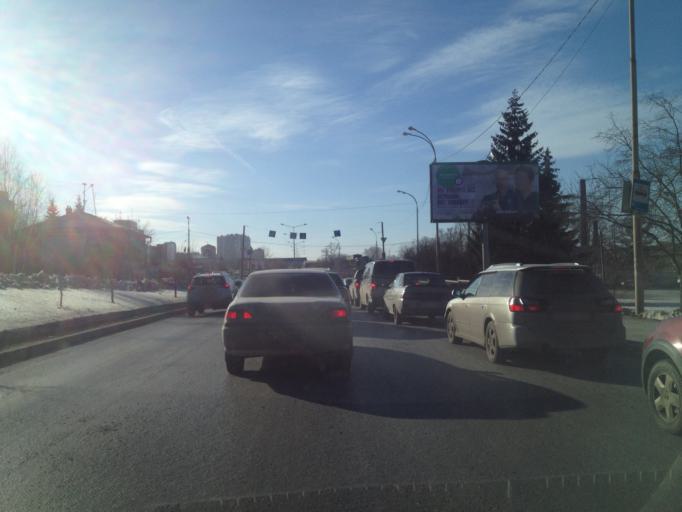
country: RU
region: Sverdlovsk
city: Yekaterinburg
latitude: 56.8397
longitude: 60.5643
